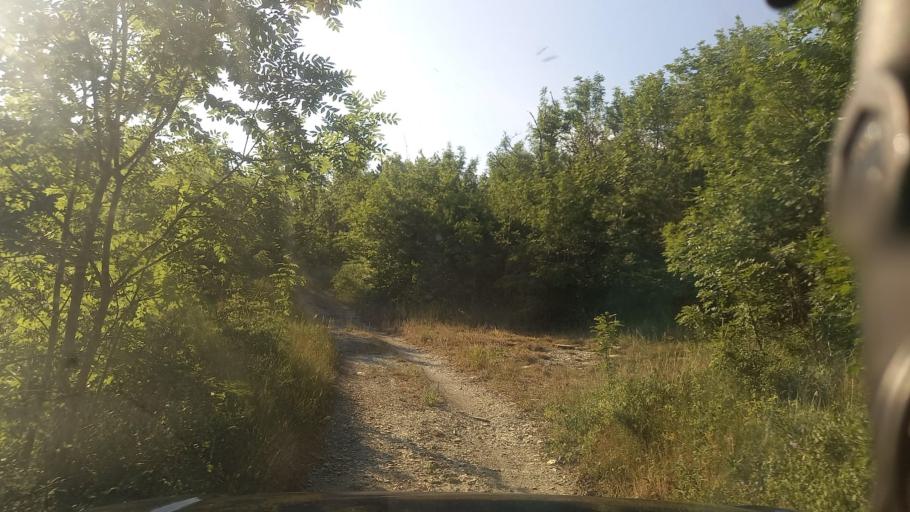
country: RU
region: Krasnodarskiy
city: Pshada
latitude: 44.5925
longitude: 38.2803
